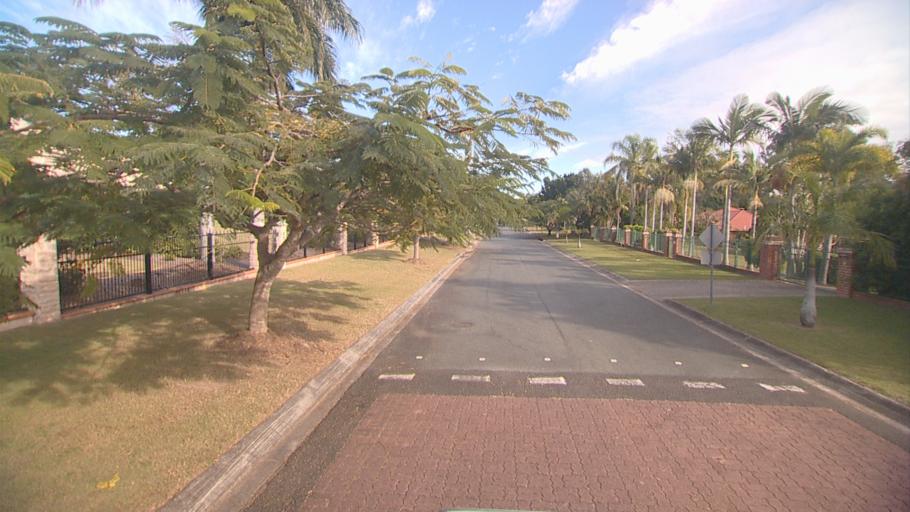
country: AU
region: Queensland
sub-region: Brisbane
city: Forest Lake
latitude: -27.6663
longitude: 153.0161
